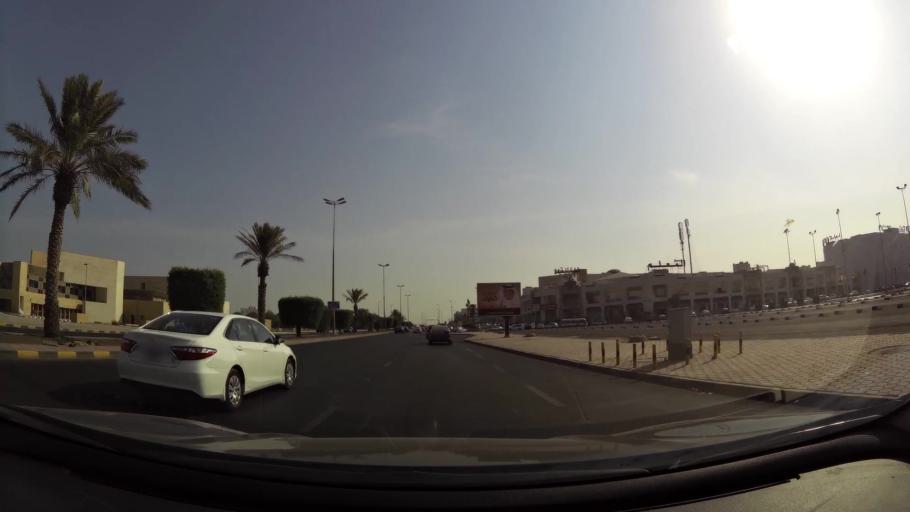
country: KW
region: Al Ahmadi
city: Al Fintas
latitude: 29.1716
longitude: 48.1002
